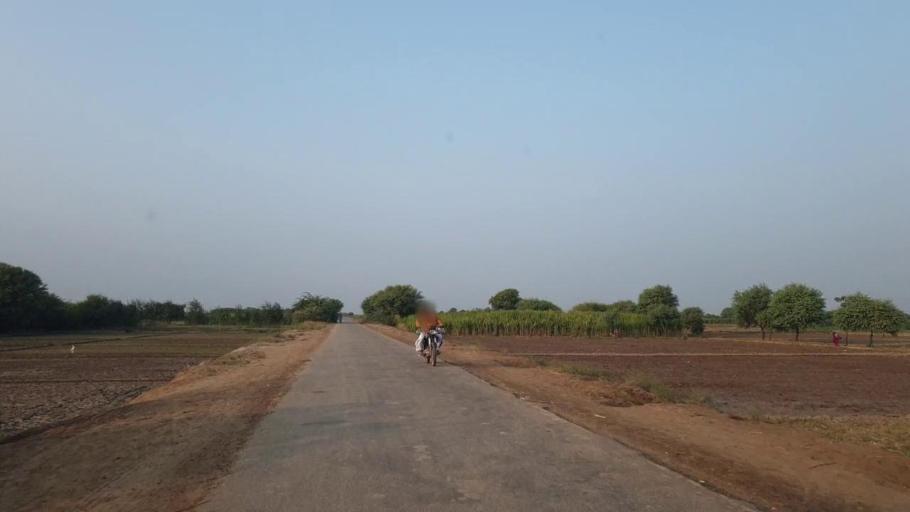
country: PK
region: Sindh
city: Tando Ghulam Ali
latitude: 25.0878
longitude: 68.9586
